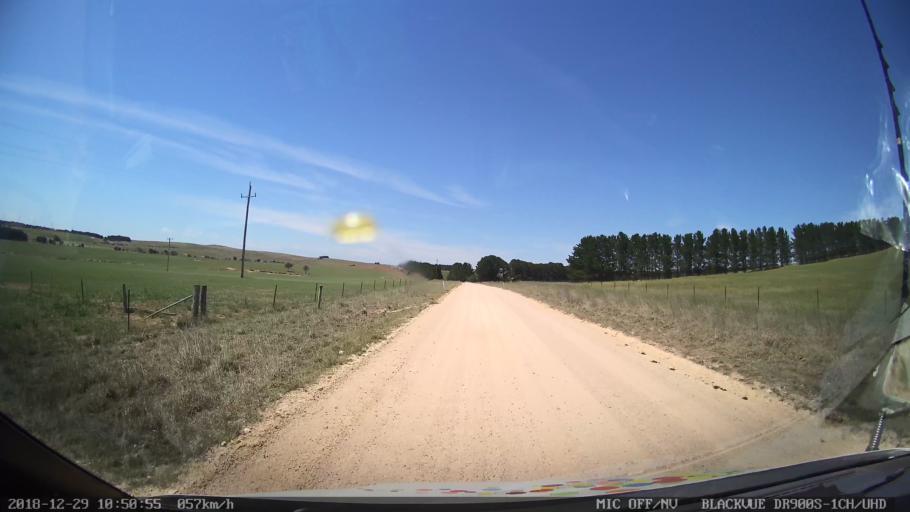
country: AU
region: New South Wales
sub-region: Palerang
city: Bungendore
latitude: -35.0852
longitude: 149.5240
